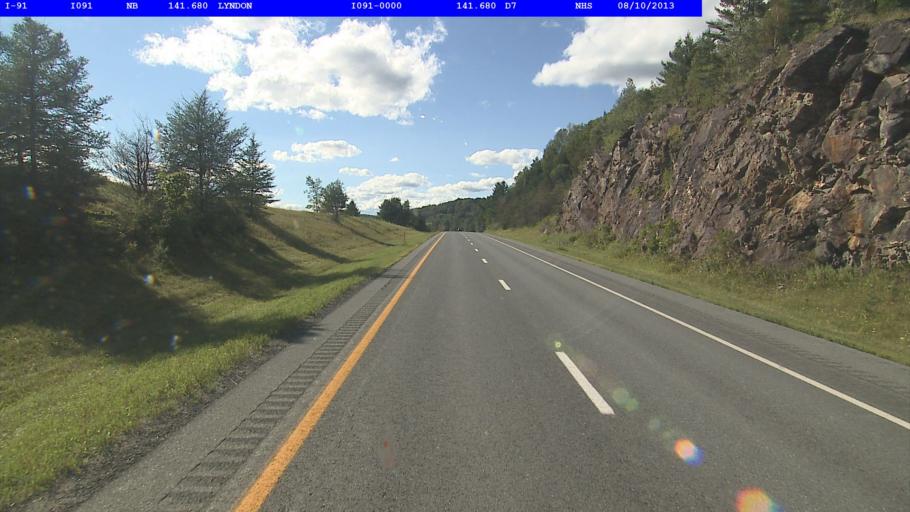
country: US
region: Vermont
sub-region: Caledonia County
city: Lyndonville
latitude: 44.5744
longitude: -72.0442
